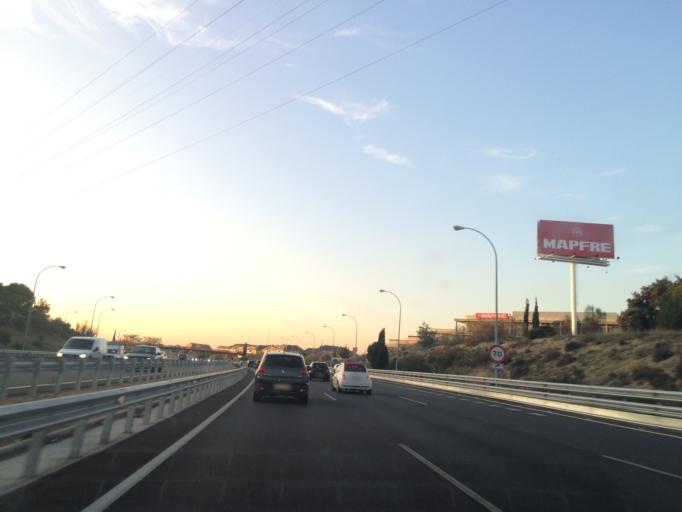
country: ES
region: Madrid
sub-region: Provincia de Madrid
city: Majadahonda
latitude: 40.4475
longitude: -3.8548
